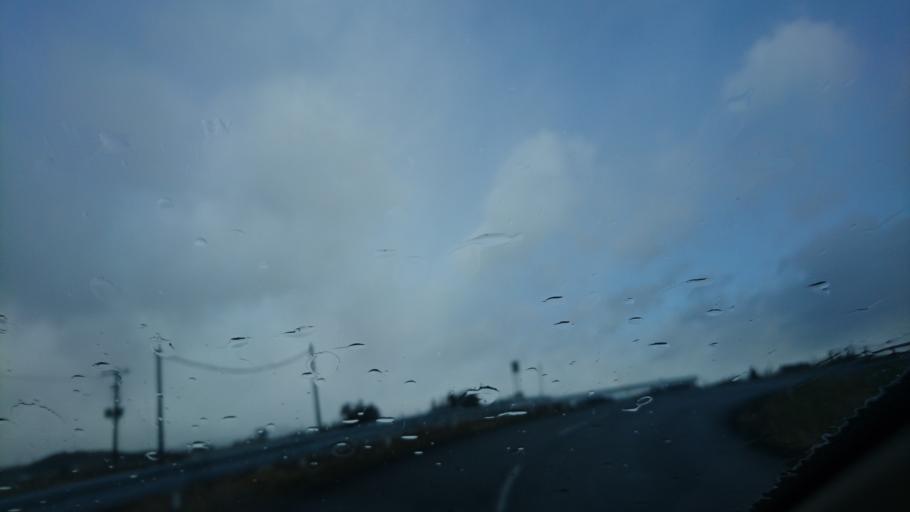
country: JP
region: Iwate
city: Ichinoseki
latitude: 38.7730
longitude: 141.0267
